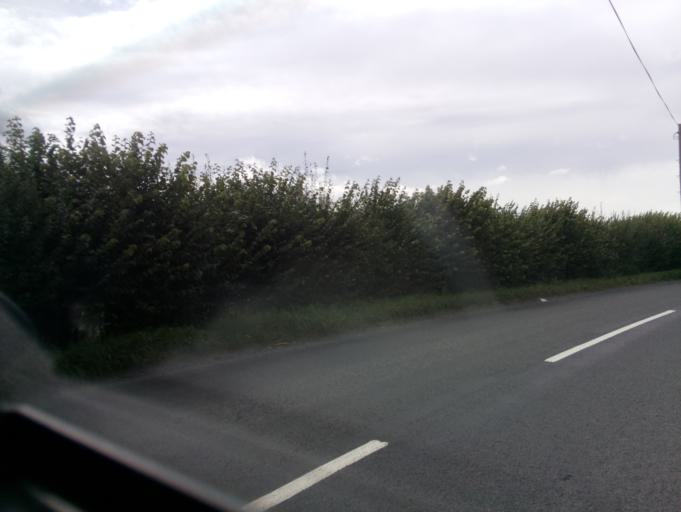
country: GB
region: England
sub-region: Somerset
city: Ilchester
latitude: 51.0463
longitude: -2.6587
